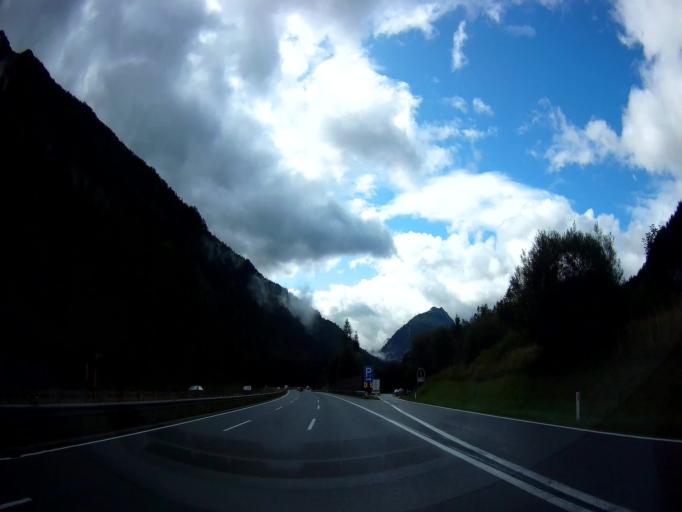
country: AT
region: Salzburg
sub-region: Politischer Bezirk Sankt Johann im Pongau
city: Flachau
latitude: 47.3193
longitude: 13.3948
